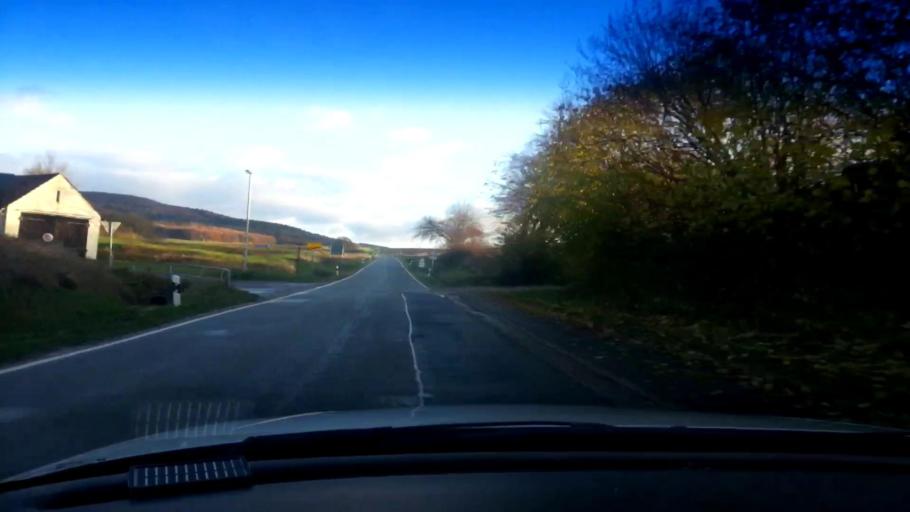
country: DE
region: Bavaria
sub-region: Upper Franconia
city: Strullendorf
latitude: 49.8572
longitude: 11.0110
